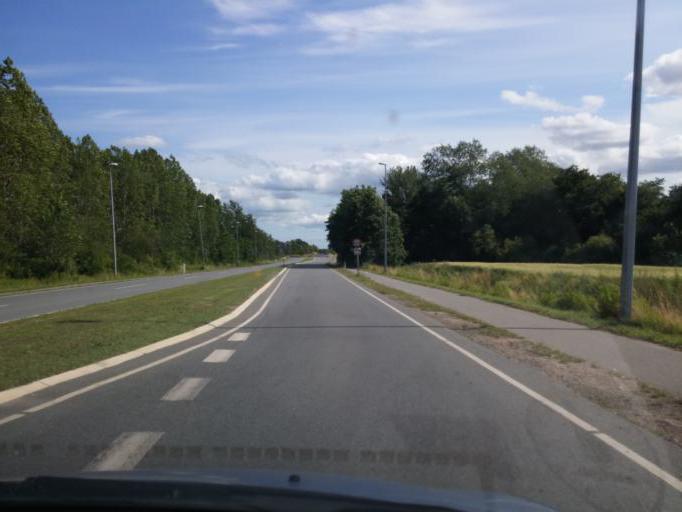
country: DK
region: South Denmark
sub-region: Kerteminde Kommune
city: Munkebo
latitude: 55.4556
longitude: 10.5373
